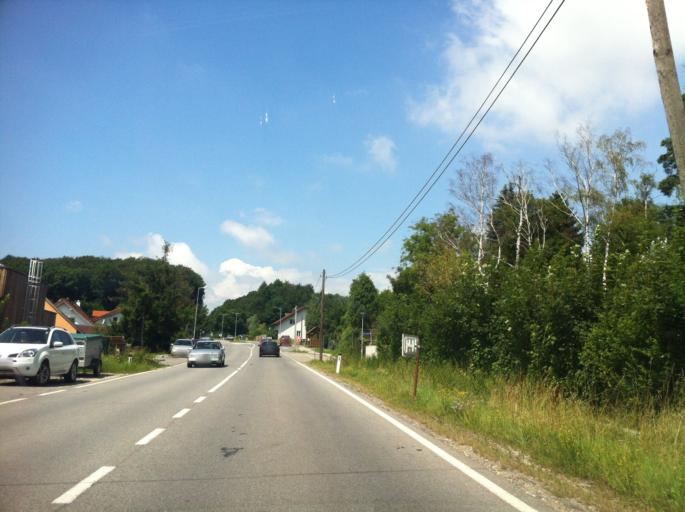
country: AT
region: Lower Austria
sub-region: Politischer Bezirk Wien-Umgebung
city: Gablitz
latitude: 48.2455
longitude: 16.1081
